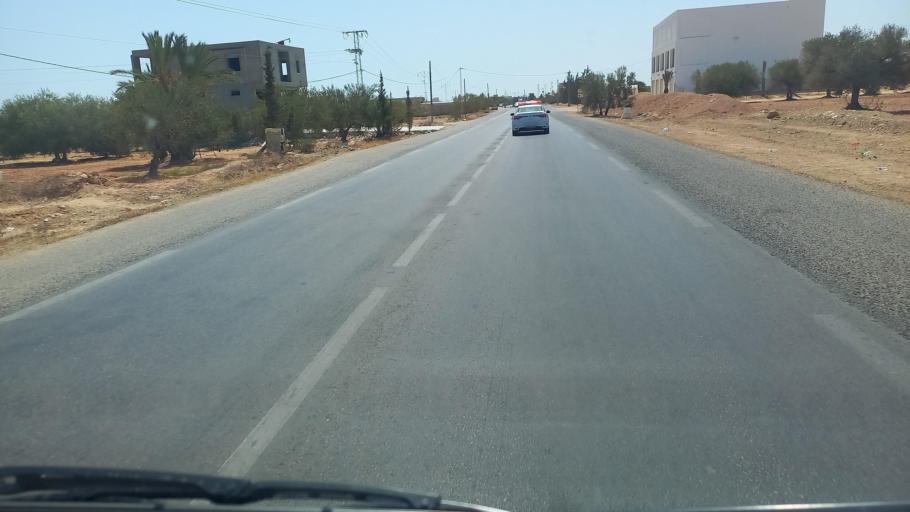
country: TN
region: Madanin
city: Houmt Souk
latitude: 33.8177
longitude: 10.8727
